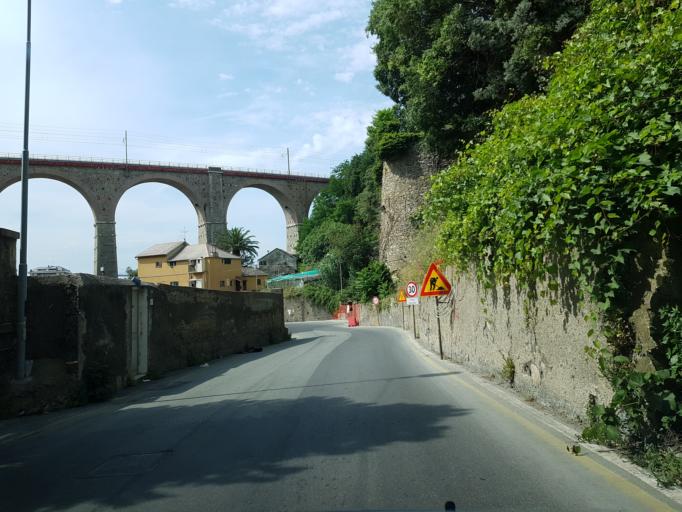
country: IT
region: Liguria
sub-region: Provincia di Genova
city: San Teodoro
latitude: 44.4364
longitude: 8.8545
